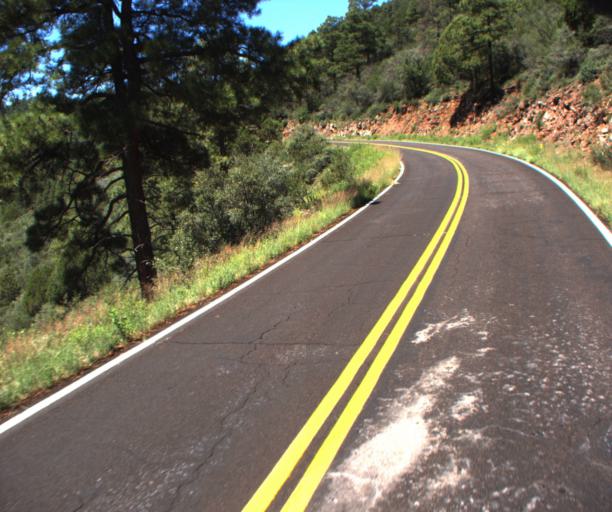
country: US
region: Arizona
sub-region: Greenlee County
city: Morenci
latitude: 33.4634
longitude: -109.3635
